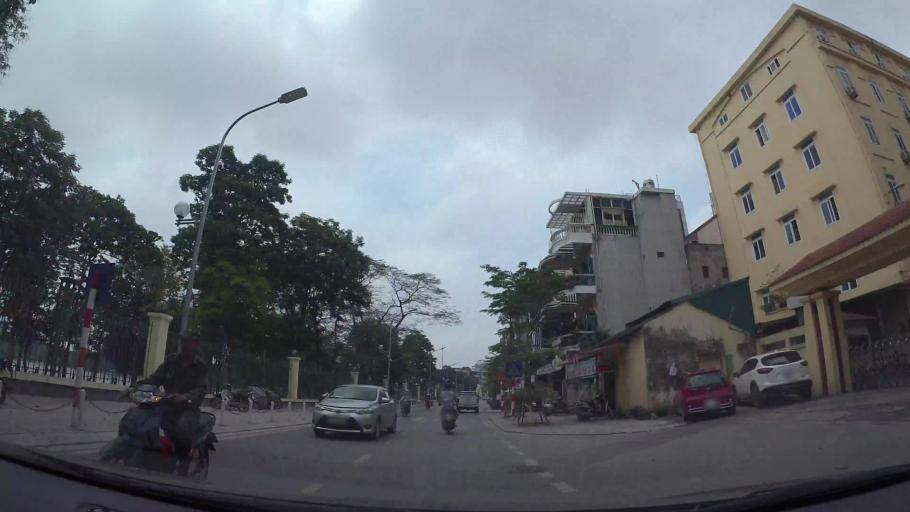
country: VN
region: Ha Noi
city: Hai BaTrung
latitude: 21.0110
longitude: 105.8459
